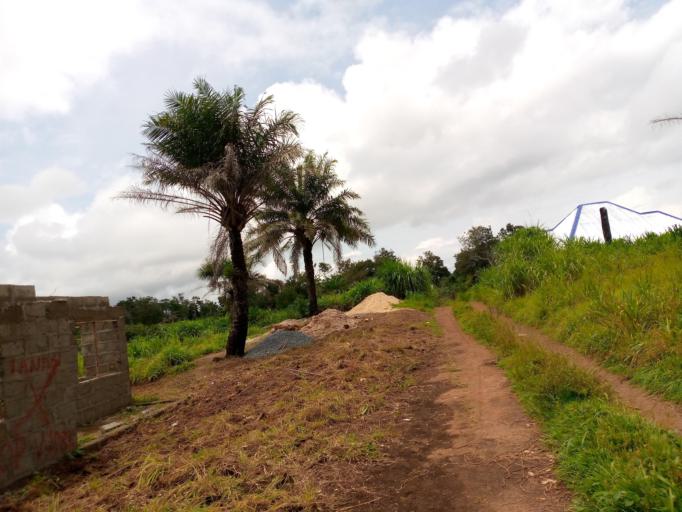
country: SL
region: Northern Province
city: Magburaka
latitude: 8.7287
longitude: -11.9327
